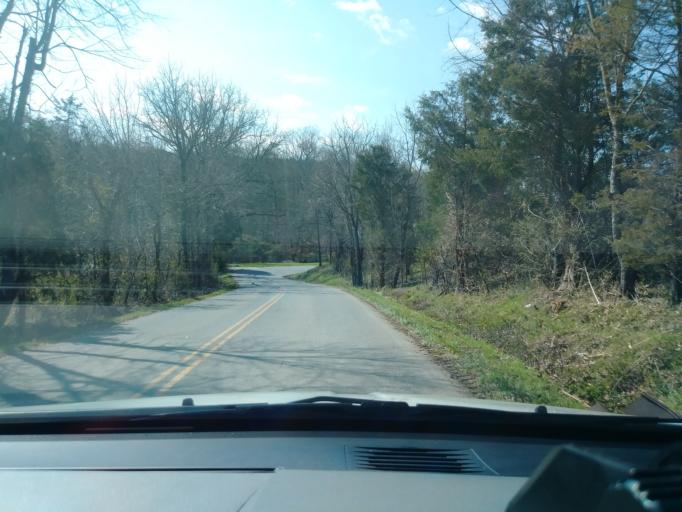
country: US
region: Tennessee
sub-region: Greene County
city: Greeneville
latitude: 36.0640
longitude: -82.7968
